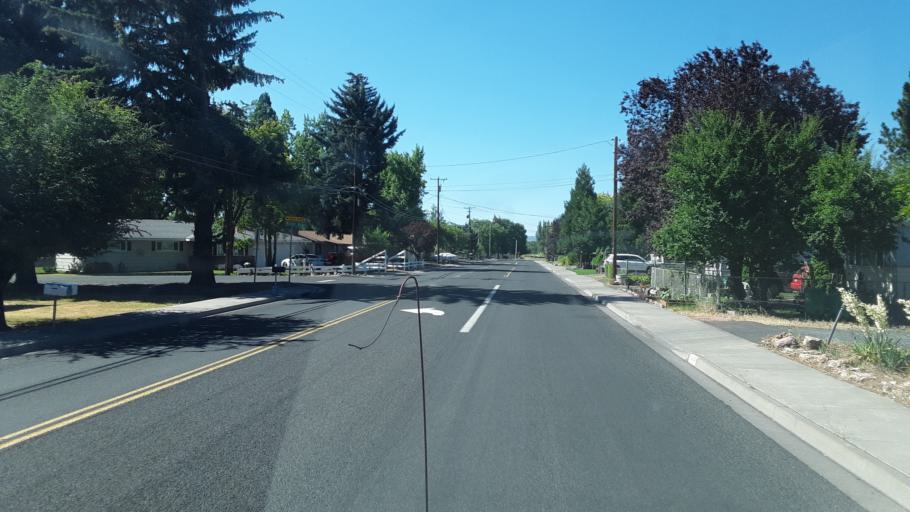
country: US
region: Oregon
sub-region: Klamath County
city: Altamont
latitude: 42.1937
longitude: -121.7178
